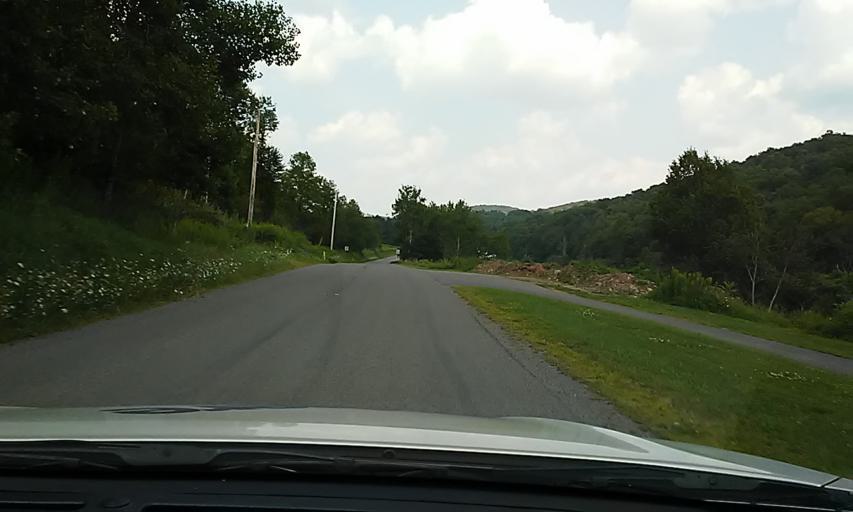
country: US
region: Pennsylvania
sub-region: Potter County
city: Coudersport
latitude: 41.7751
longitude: -77.9297
